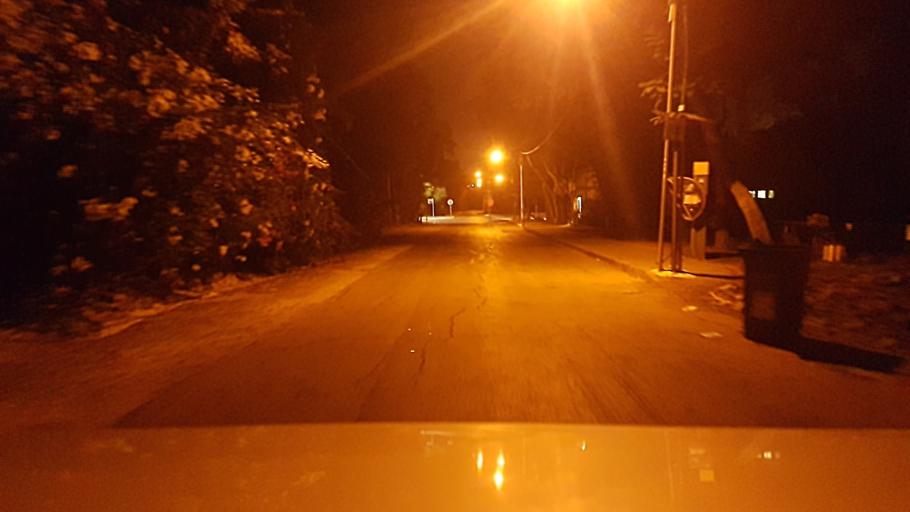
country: IL
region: Central District
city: Nehalim
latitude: 32.0765
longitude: 34.9242
